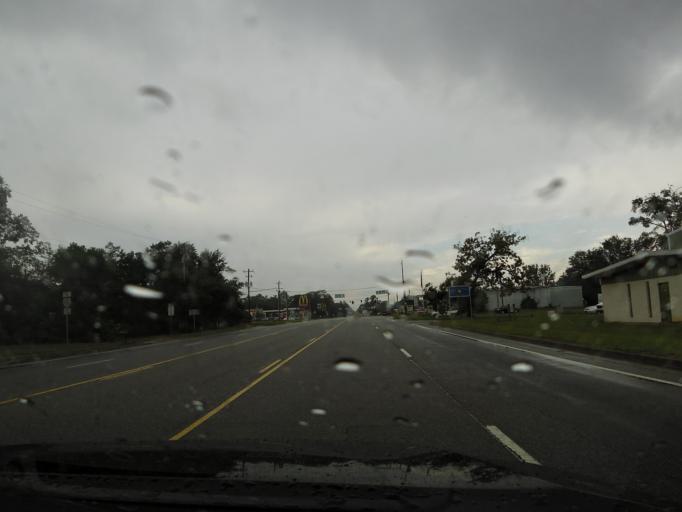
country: US
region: Georgia
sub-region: Wayne County
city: Jesup
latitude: 31.5934
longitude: -81.8686
